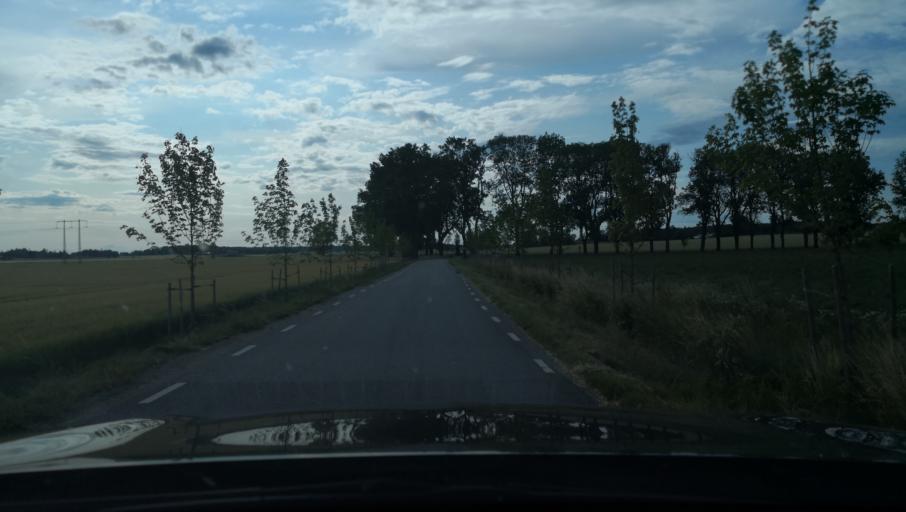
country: SE
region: Uppsala
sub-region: Enkopings Kommun
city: Orsundsbro
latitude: 59.6972
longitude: 17.3223
